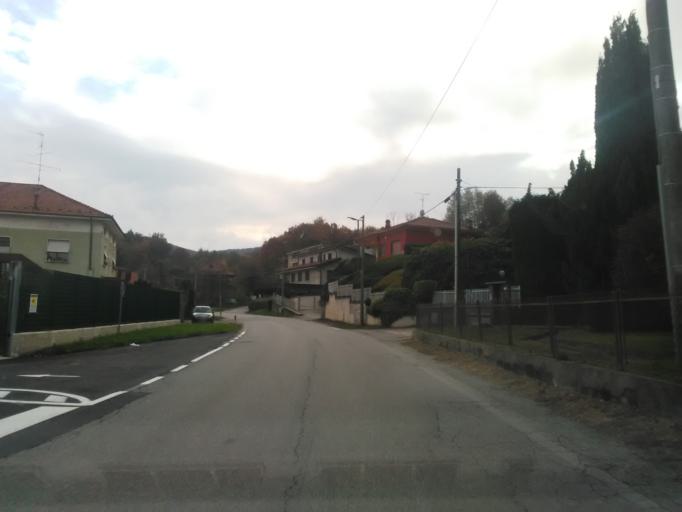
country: IT
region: Piedmont
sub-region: Provincia di Novara
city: Pogno
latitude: 45.7553
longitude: 8.3805
